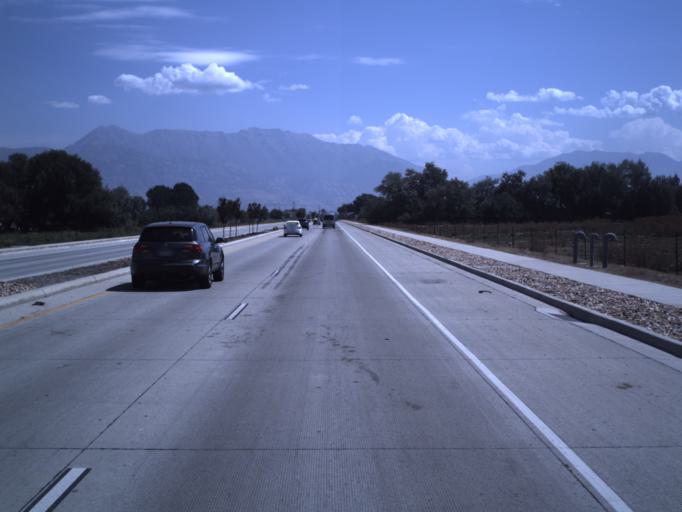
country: US
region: Utah
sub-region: Utah County
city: Saratoga Springs
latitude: 40.3762
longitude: -111.8947
